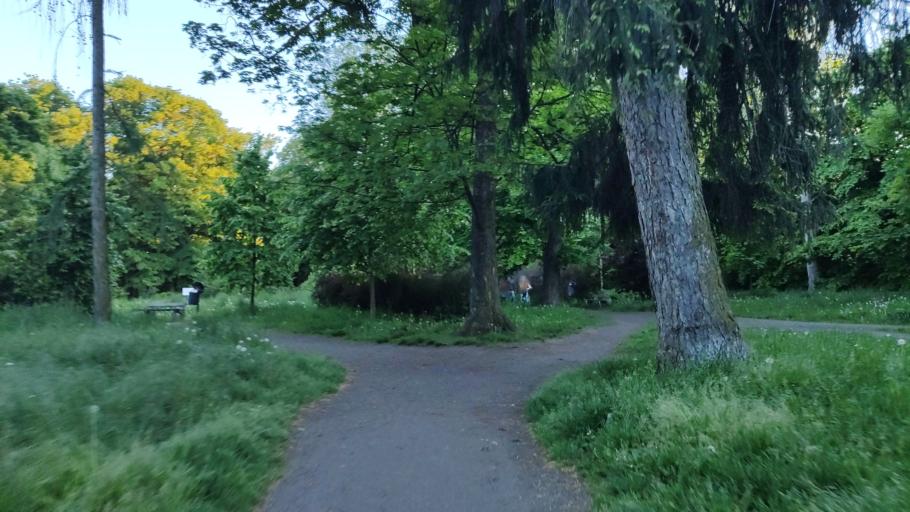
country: PL
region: Lower Silesian Voivodeship
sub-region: Powiat wroclawski
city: Wroclaw
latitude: 51.0792
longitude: 17.0257
